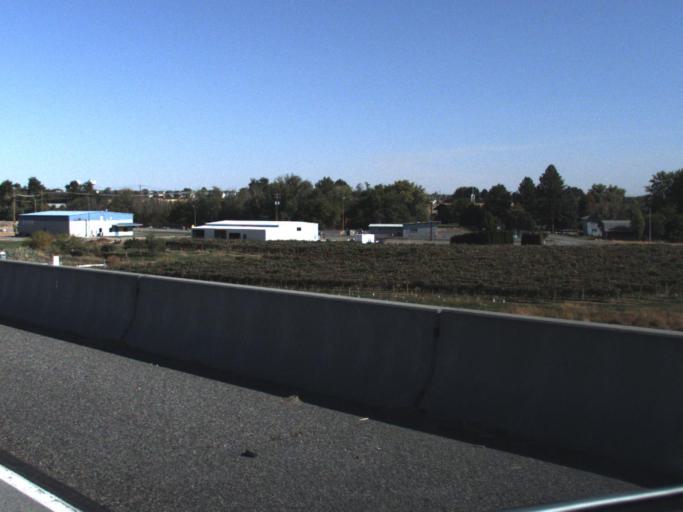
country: US
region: Washington
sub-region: Benton County
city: Richland
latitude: 46.2678
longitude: -119.2366
